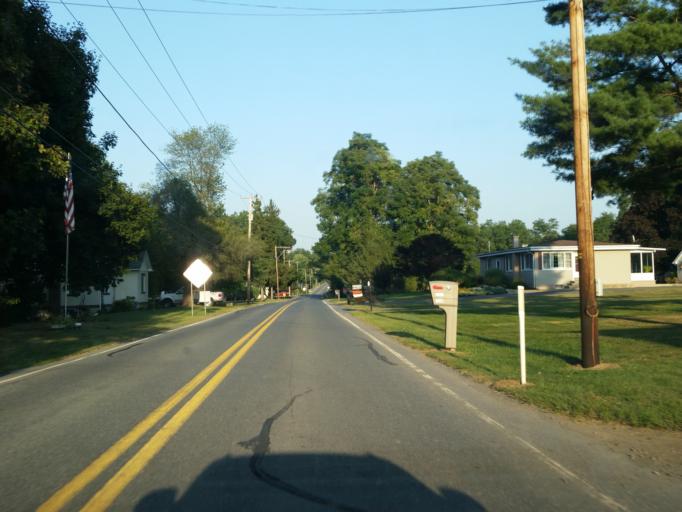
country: US
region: Pennsylvania
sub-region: Lebanon County
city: Cleona
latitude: 40.3693
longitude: -76.4800
